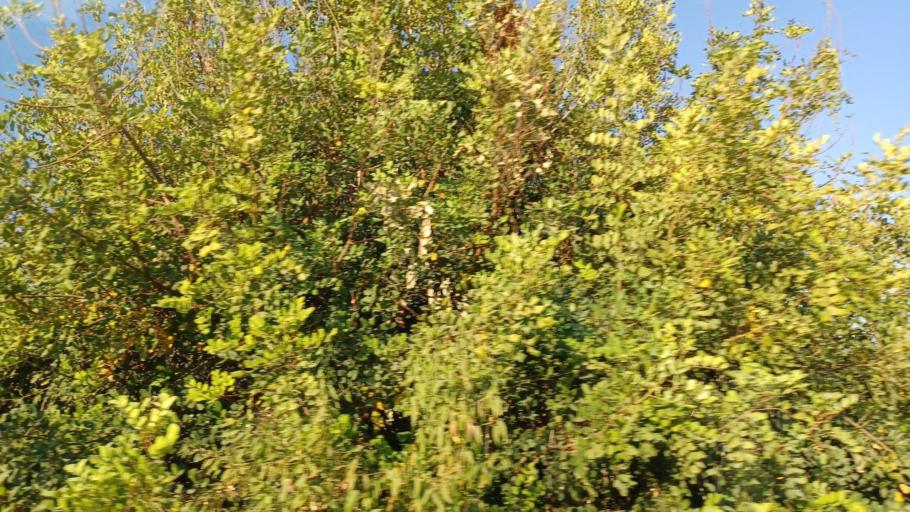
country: CY
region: Limassol
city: Pissouri
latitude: 34.7134
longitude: 32.6745
